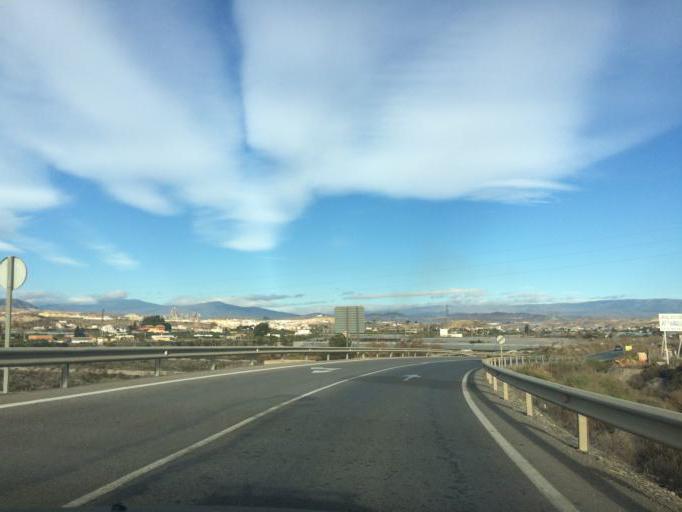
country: ES
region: Andalusia
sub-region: Provincia de Almeria
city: Pechina
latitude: 36.9163
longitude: -2.4441
